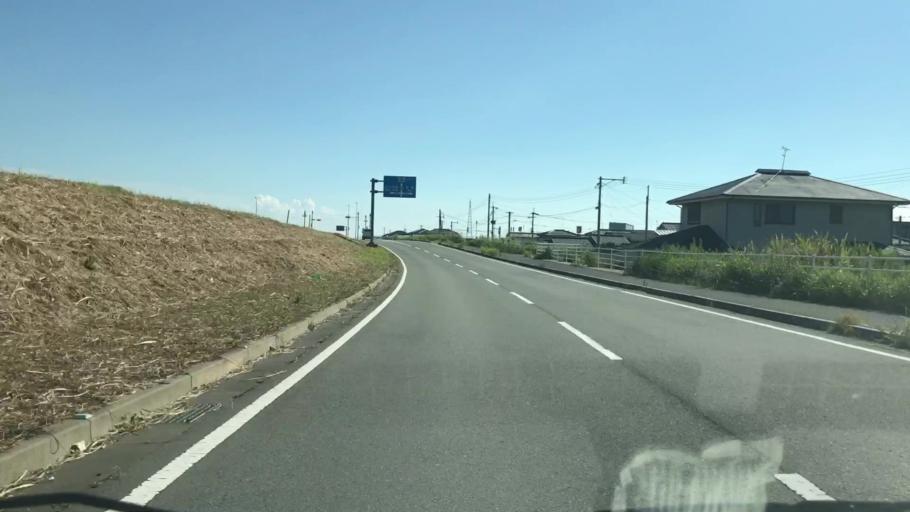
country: JP
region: Saga Prefecture
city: Okawa
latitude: 33.2384
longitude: 130.3808
